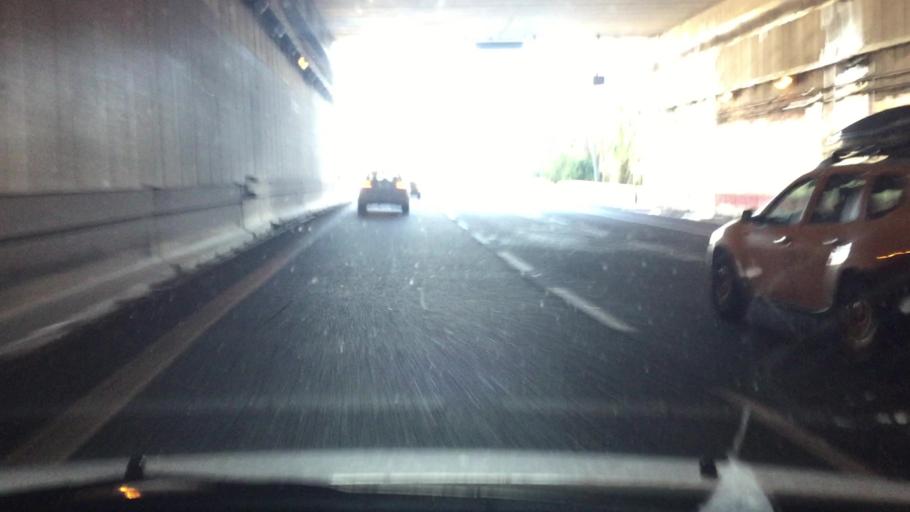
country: VA
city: Vatican City
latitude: 41.9781
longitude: 12.4282
